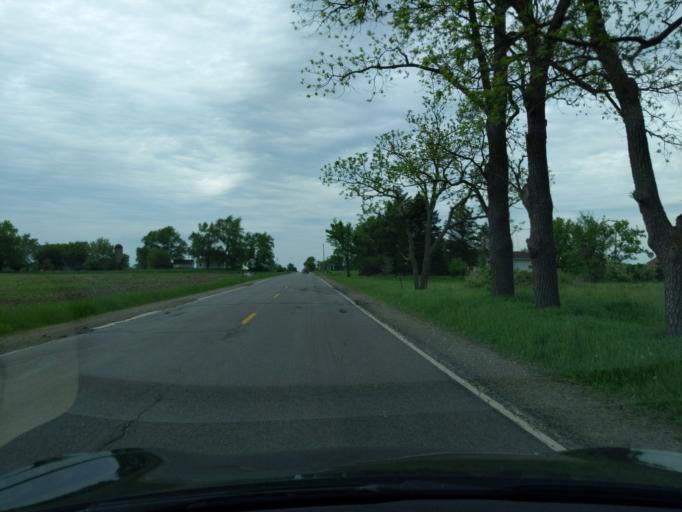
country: US
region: Michigan
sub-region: Ingham County
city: Mason
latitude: 42.6257
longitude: -84.3639
